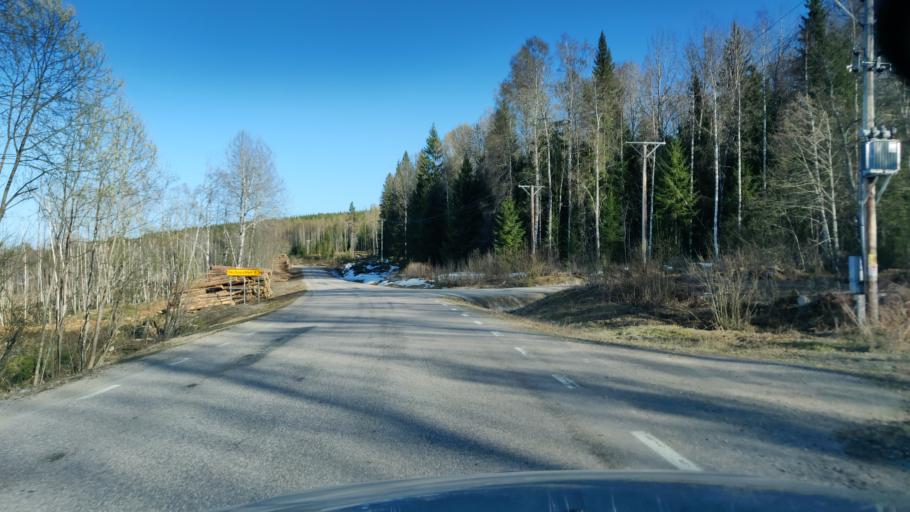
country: SE
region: Vaermland
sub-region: Munkfors Kommun
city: Munkfors
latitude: 59.9699
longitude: 13.4212
